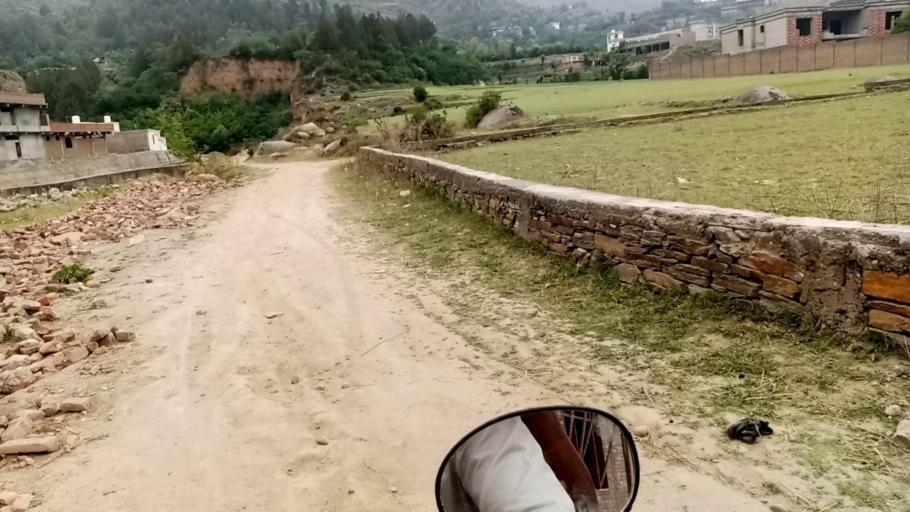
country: PK
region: Khyber Pakhtunkhwa
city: Saidu Sharif
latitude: 34.7536
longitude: 72.3871
